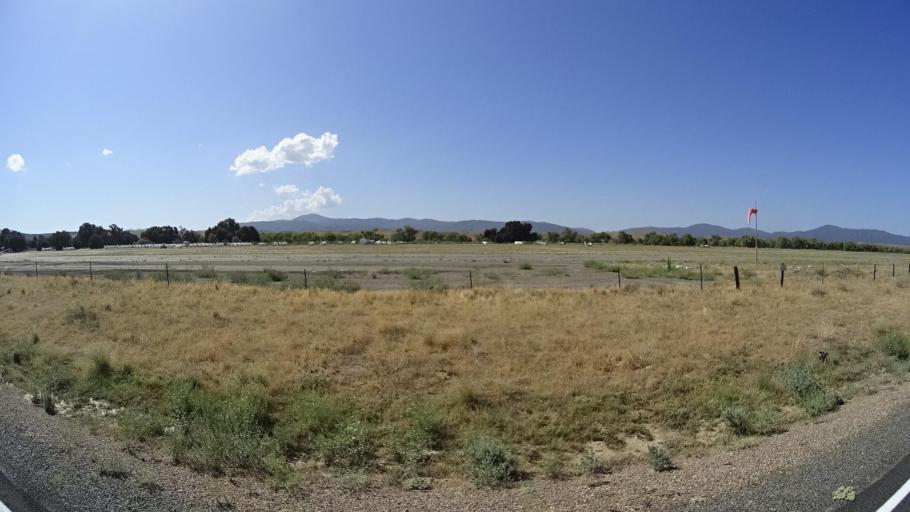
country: US
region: California
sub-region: San Diego County
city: Julian
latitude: 33.2850
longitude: -116.6695
